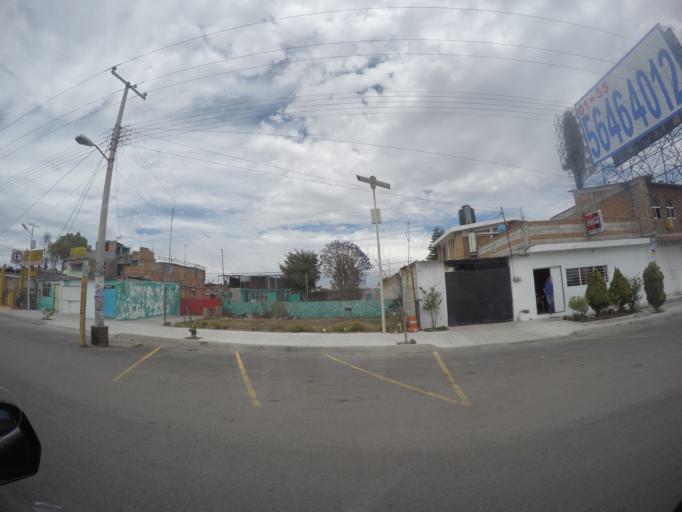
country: MX
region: Queretaro
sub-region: San Juan del Rio
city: Paso de Mata
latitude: 20.3341
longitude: -99.9390
